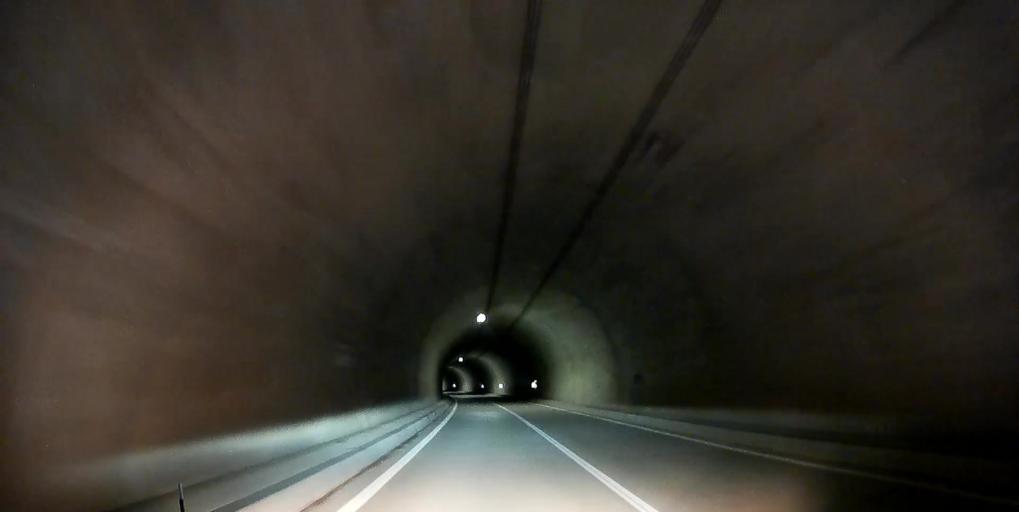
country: JP
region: Hokkaido
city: Iwanai
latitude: 42.3191
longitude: 139.7723
